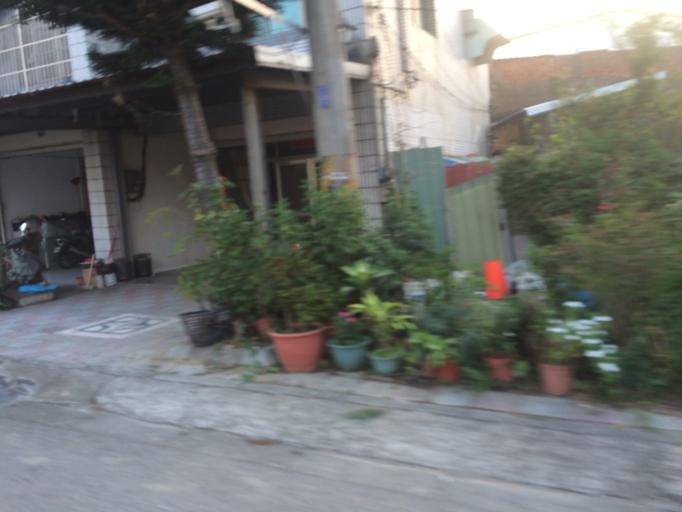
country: TW
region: Taiwan
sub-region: Hsinchu
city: Hsinchu
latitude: 24.7282
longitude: 120.9173
